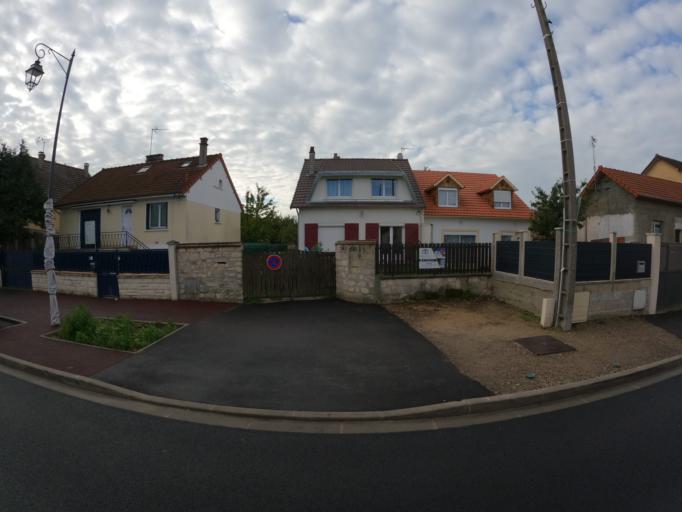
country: FR
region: Ile-de-France
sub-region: Departement de Seine-Saint-Denis
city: Montfermeil
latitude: 48.9035
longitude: 2.5905
